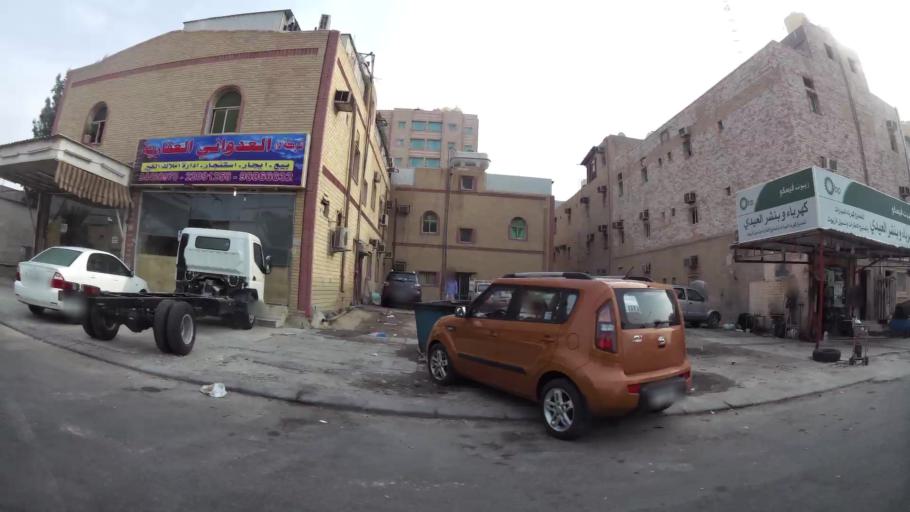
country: KW
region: Al Farwaniyah
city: Al Farwaniyah
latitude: 29.2974
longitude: 47.9734
